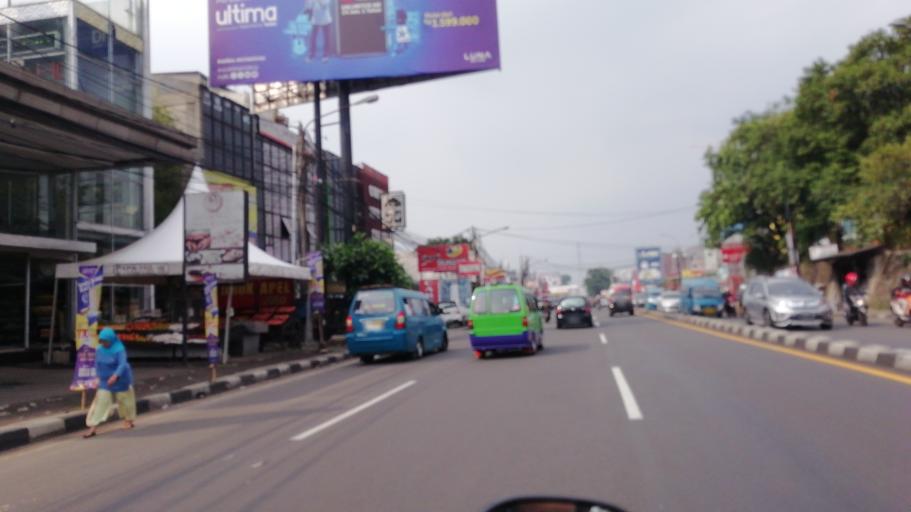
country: ID
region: West Java
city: Bogor
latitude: -6.5674
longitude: 106.8095
